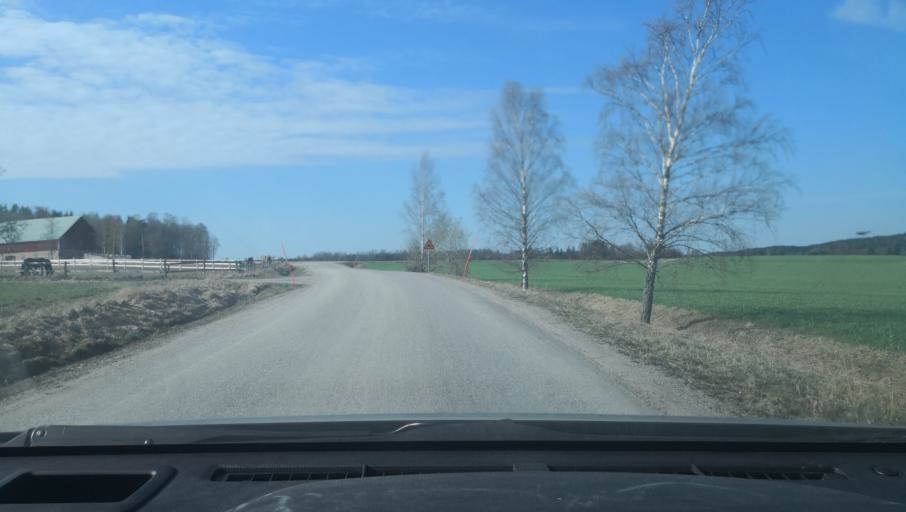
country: SE
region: Uppsala
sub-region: Heby Kommun
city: Morgongava
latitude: 59.8443
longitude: 16.9143
